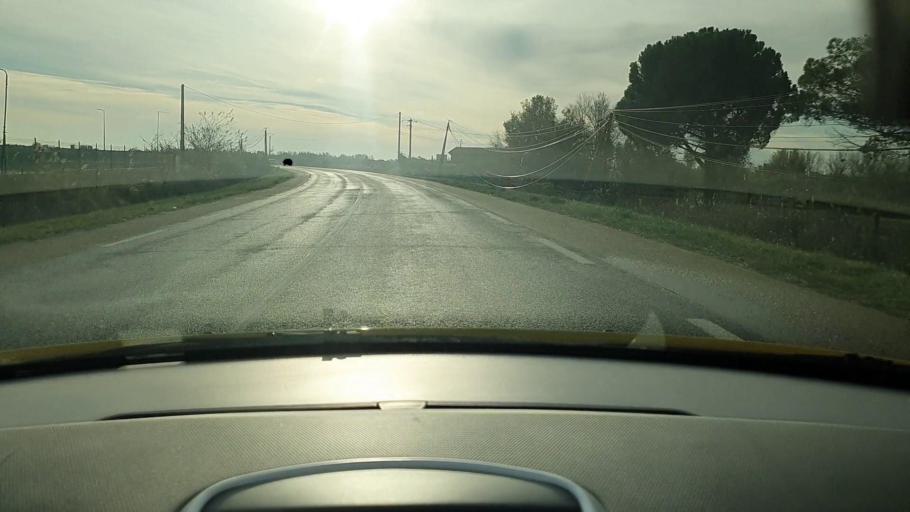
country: FR
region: Languedoc-Roussillon
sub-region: Departement du Gard
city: Bellegarde
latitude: 43.7344
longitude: 4.5230
